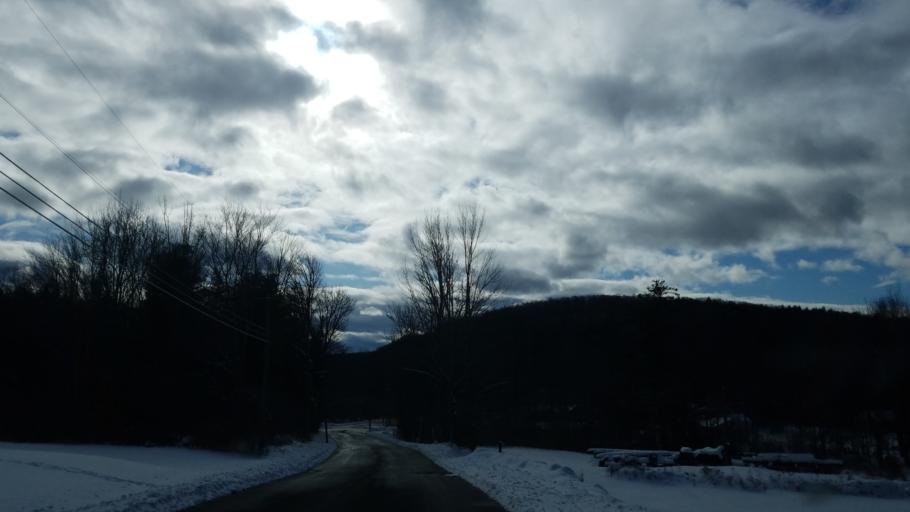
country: US
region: Connecticut
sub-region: Litchfield County
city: Winchester Center
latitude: 41.9645
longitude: -73.1198
